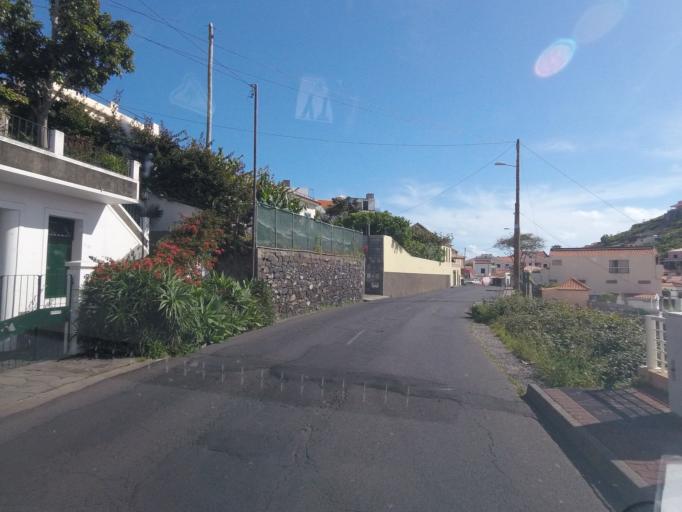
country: PT
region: Madeira
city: Camara de Lobos
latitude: 32.6547
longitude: -16.9705
